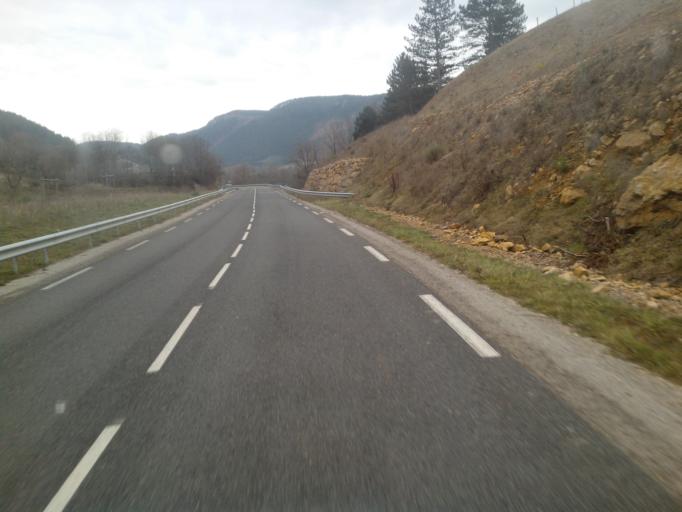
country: FR
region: Languedoc-Roussillon
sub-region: Departement de la Lozere
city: Mende
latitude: 44.4671
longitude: 3.5124
